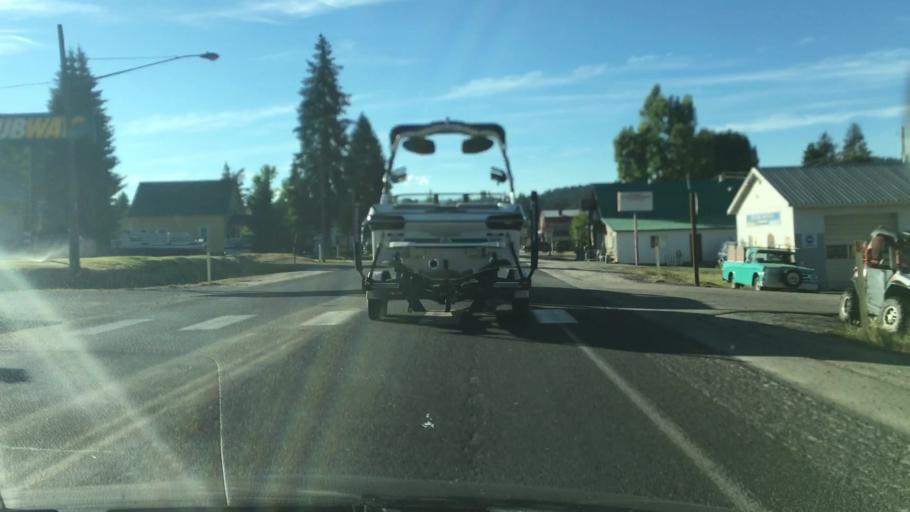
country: US
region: Idaho
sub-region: Valley County
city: Cascade
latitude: 44.5133
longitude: -116.0392
